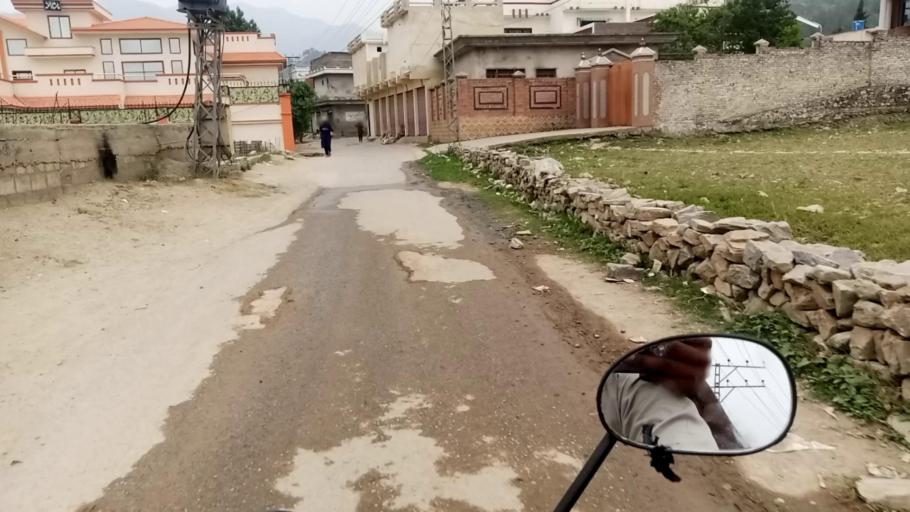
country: PK
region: Khyber Pakhtunkhwa
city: Saidu Sharif
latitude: 34.7548
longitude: 72.3845
